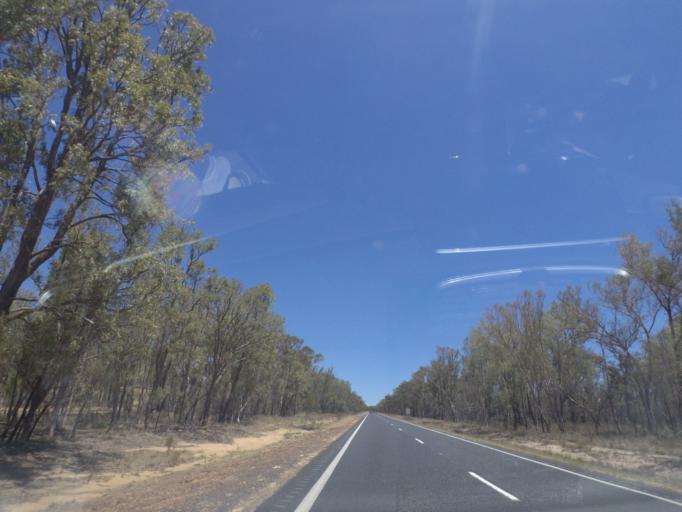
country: AU
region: New South Wales
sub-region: Warrumbungle Shire
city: Coonabarabran
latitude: -31.1696
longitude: 149.3619
